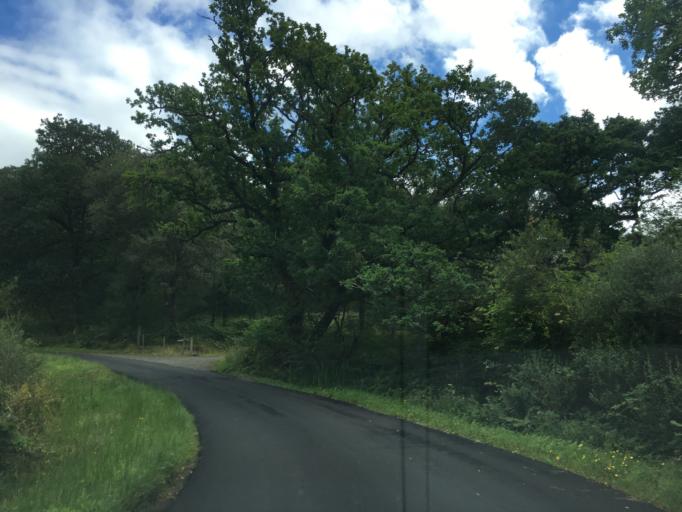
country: GB
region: Scotland
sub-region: Argyll and Bute
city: Oban
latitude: 56.3419
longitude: -5.1984
